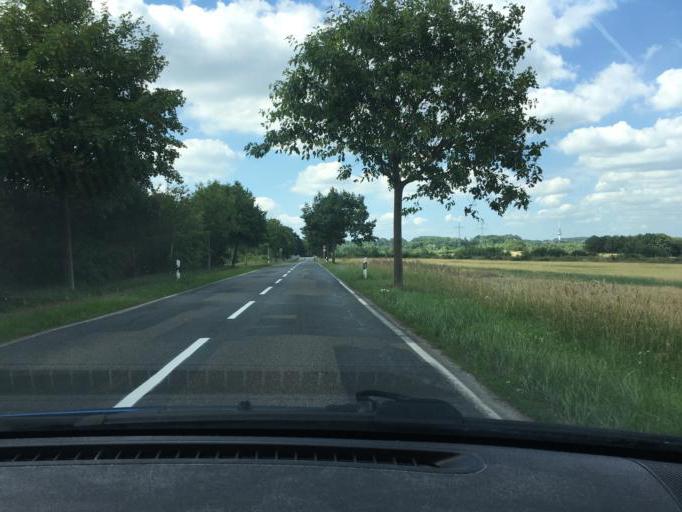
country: DE
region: Lower Saxony
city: Buchholz in der Nordheide
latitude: 53.3703
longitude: 9.8678
